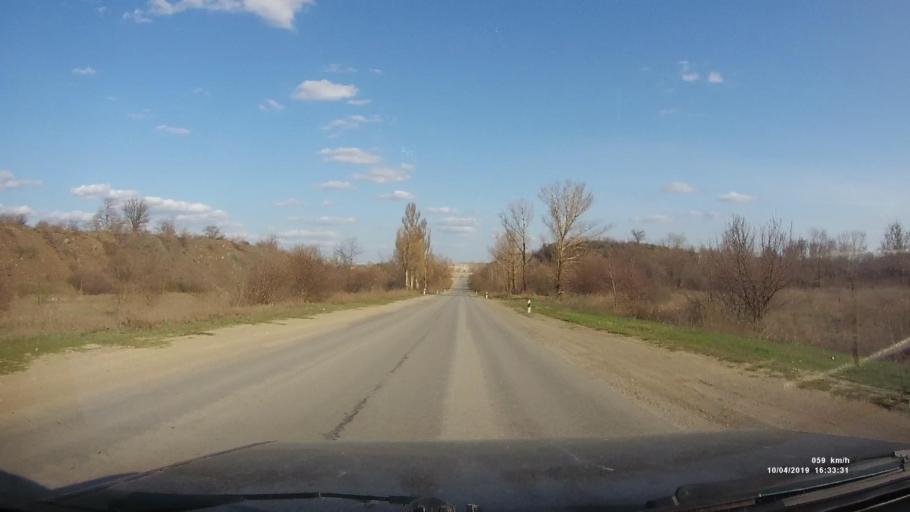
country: RU
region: Rostov
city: Staraya Stanitsa
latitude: 48.2408
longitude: 40.3985
